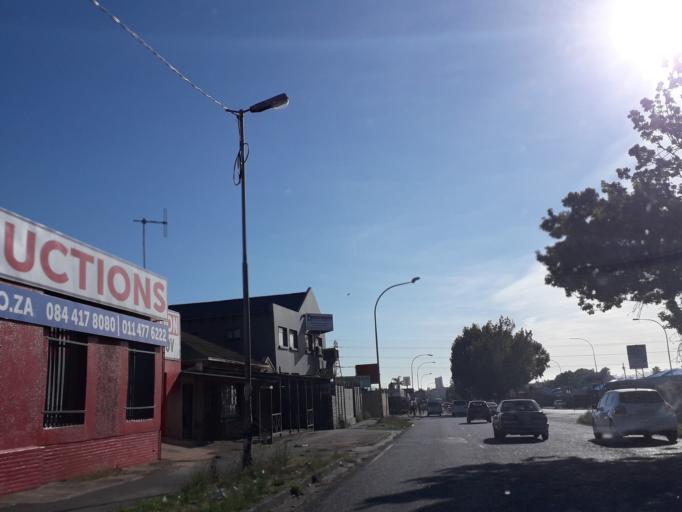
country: ZA
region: Gauteng
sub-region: City of Johannesburg Metropolitan Municipality
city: Roodepoort
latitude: -26.1746
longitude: 27.9535
